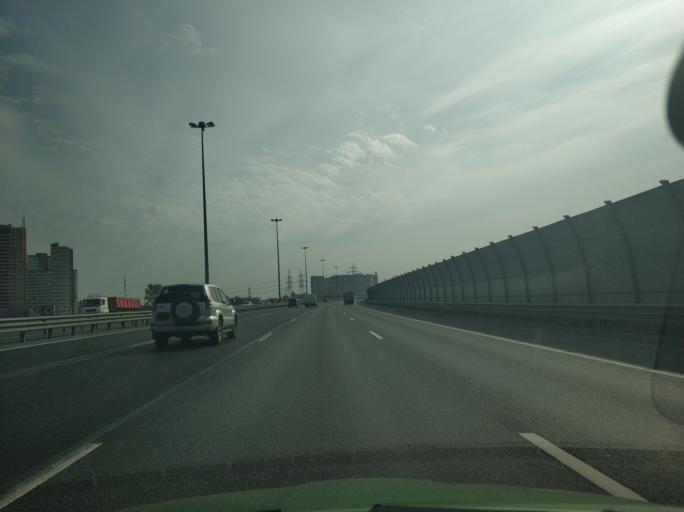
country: RU
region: St.-Petersburg
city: Grazhdanka
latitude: 60.0480
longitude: 30.4225
